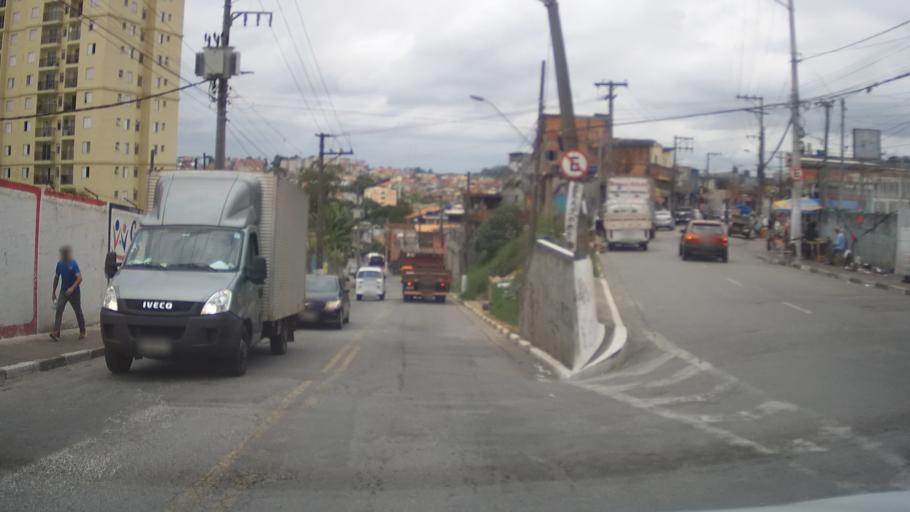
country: BR
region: Sao Paulo
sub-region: Itaquaquecetuba
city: Itaquaquecetuba
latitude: -23.4526
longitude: -46.4051
